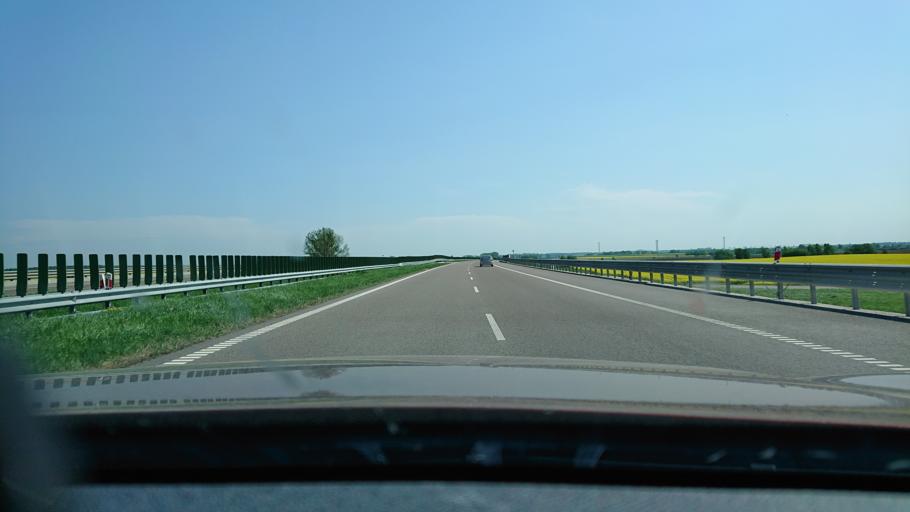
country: PL
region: Subcarpathian Voivodeship
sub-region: Powiat przemyski
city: Stubno
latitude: 49.9400
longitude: 22.9484
